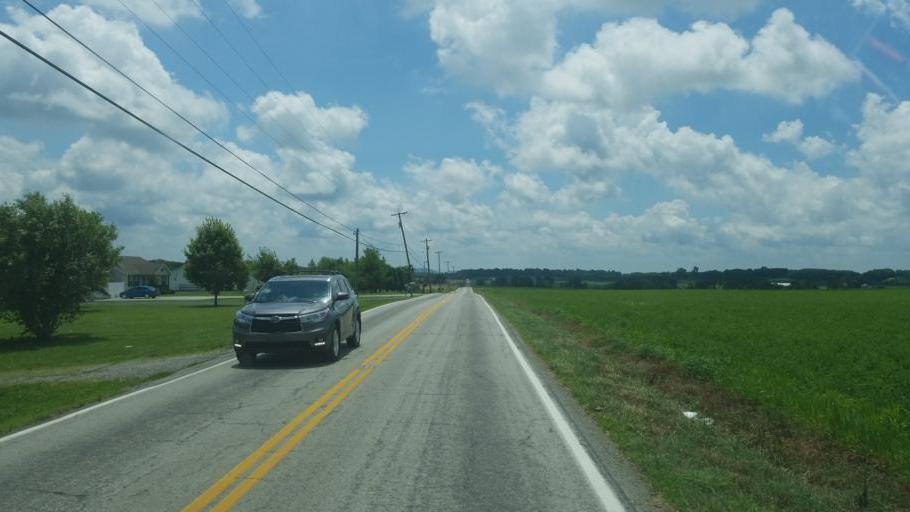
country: US
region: Ohio
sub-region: Highland County
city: Greenfield
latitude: 39.2587
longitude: -83.4425
